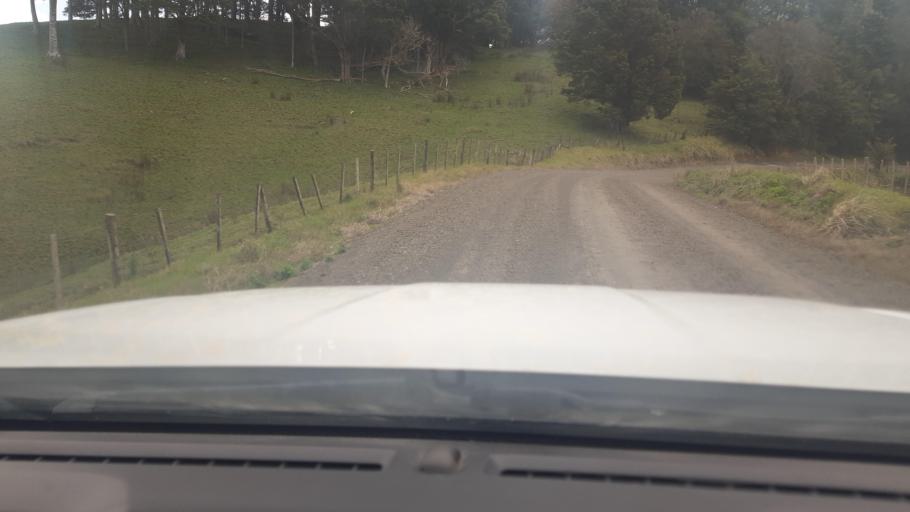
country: NZ
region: Northland
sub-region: Far North District
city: Kaitaia
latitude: -35.0824
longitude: 173.3213
